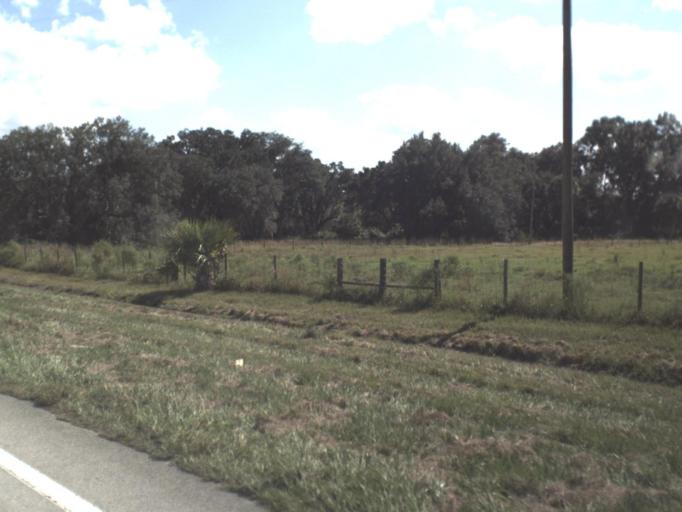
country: US
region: Florida
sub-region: Okeechobee County
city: Okeechobee
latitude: 27.3833
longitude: -80.9947
